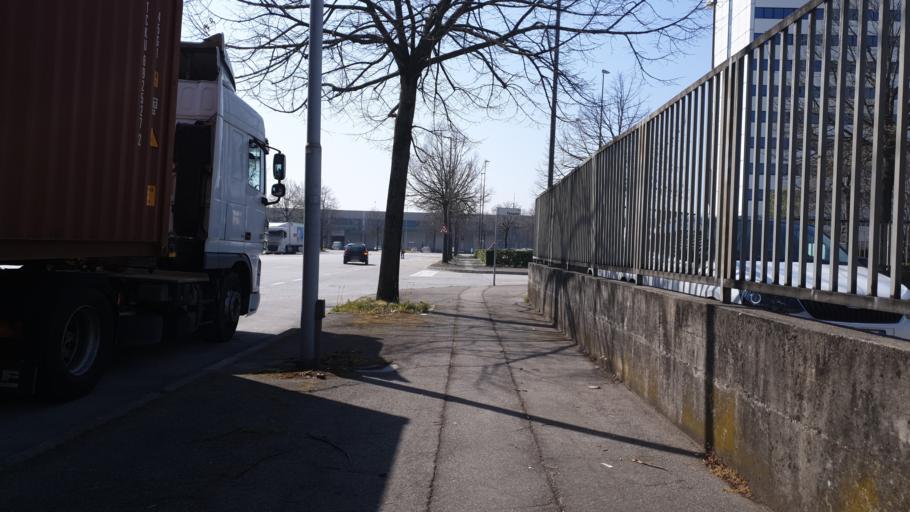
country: IT
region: Veneto
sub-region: Provincia di Padova
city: Ponte San Nicolo
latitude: 45.3893
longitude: 11.9295
